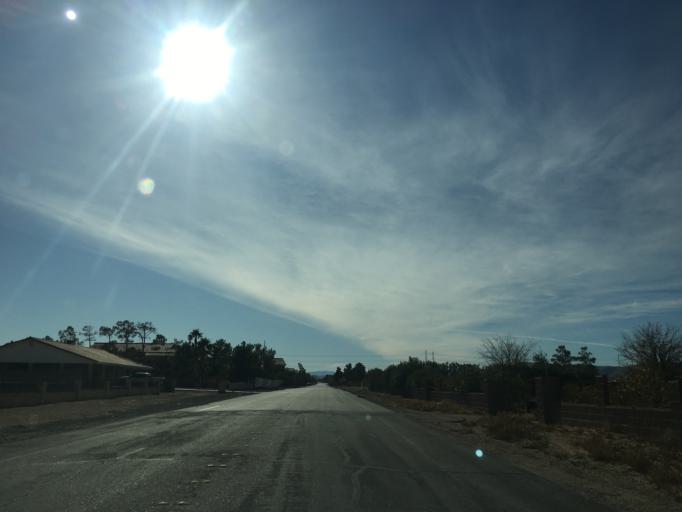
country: US
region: Nevada
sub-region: Clark County
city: Enterprise
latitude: 36.0083
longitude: -115.1658
